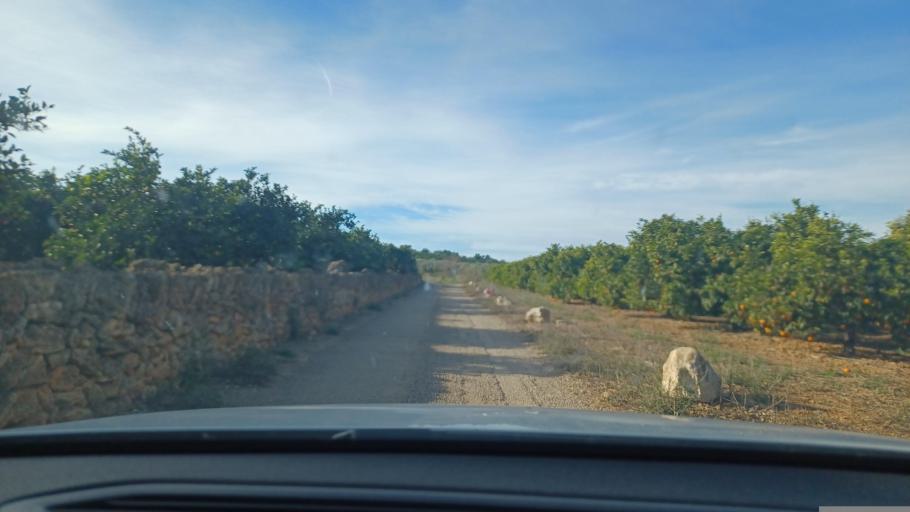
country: ES
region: Catalonia
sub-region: Provincia de Tarragona
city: Santa Barbara
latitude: 40.6853
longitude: 0.5001
